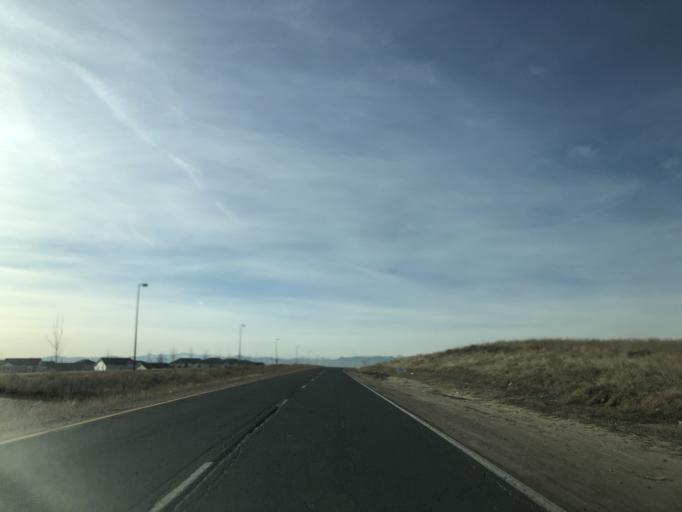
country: US
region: Colorado
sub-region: Adams County
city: Aurora
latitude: 39.7985
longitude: -104.7462
